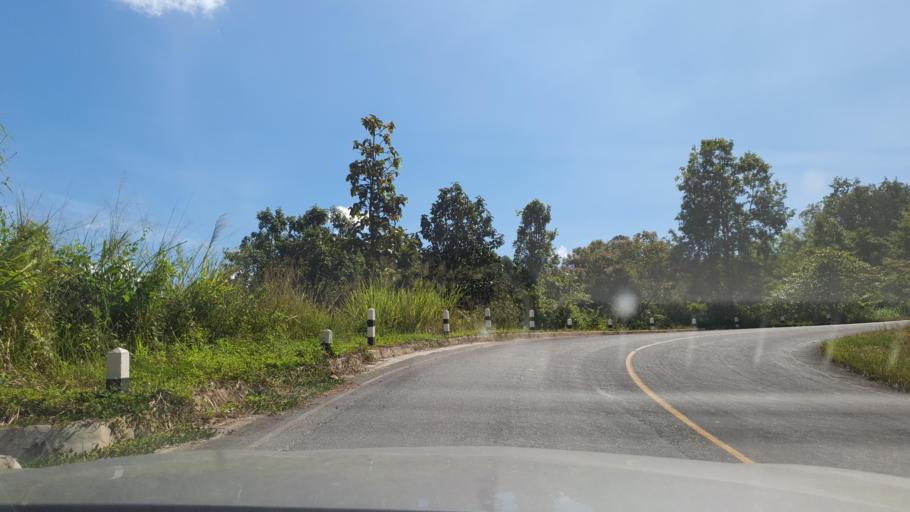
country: TH
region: Chiang Mai
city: Phrao
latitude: 19.3588
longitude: 99.2745
